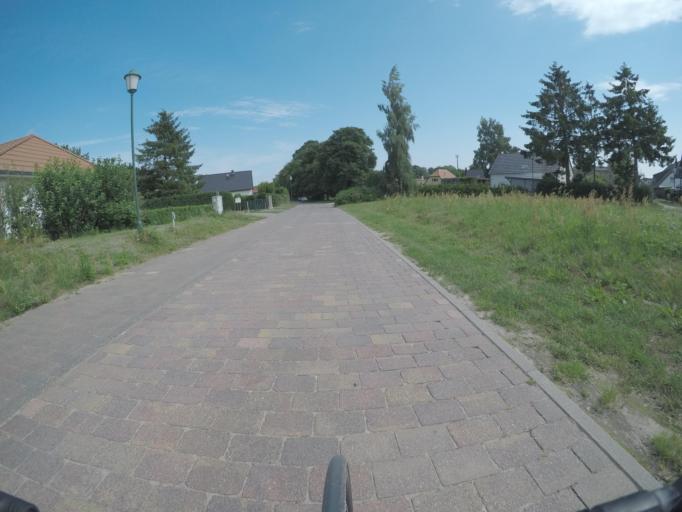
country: DE
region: Mecklenburg-Vorpommern
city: Rambin
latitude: 54.3558
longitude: 13.2008
